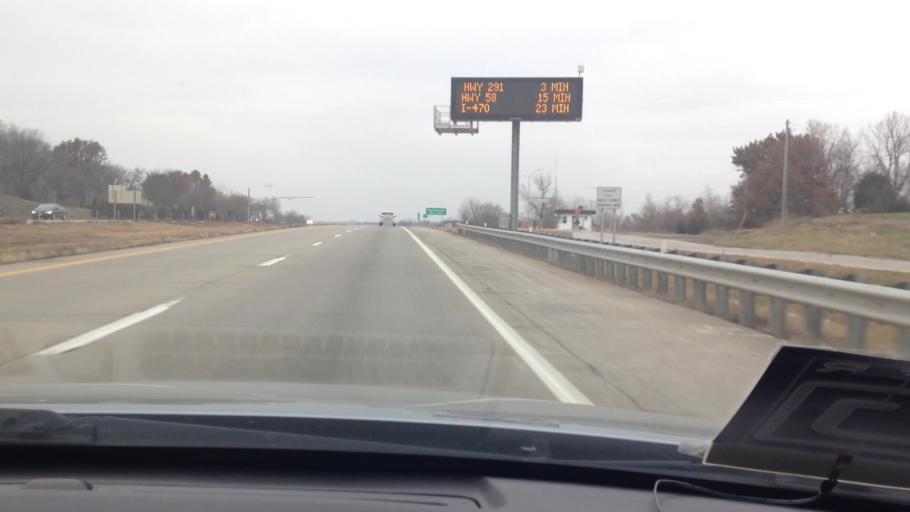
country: US
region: Missouri
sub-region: Cass County
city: Harrisonville
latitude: 38.6267
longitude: -94.3498
